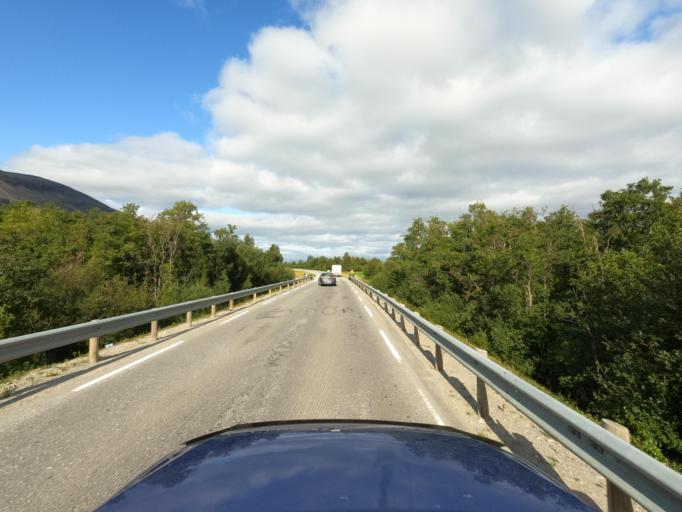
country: NO
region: Finnmark Fylke
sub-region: Porsanger
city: Lakselv
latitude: 70.0659
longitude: 24.9292
